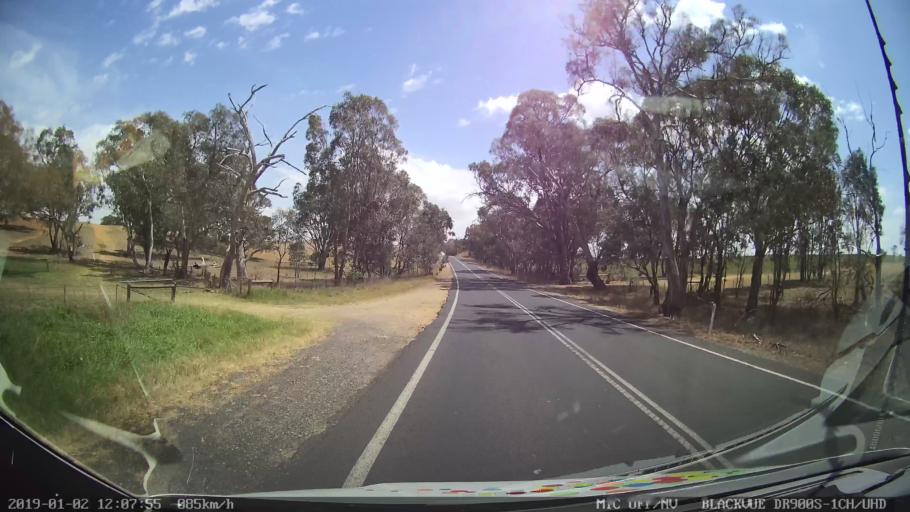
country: AU
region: New South Wales
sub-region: Young
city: Young
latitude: -34.4900
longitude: 148.2792
